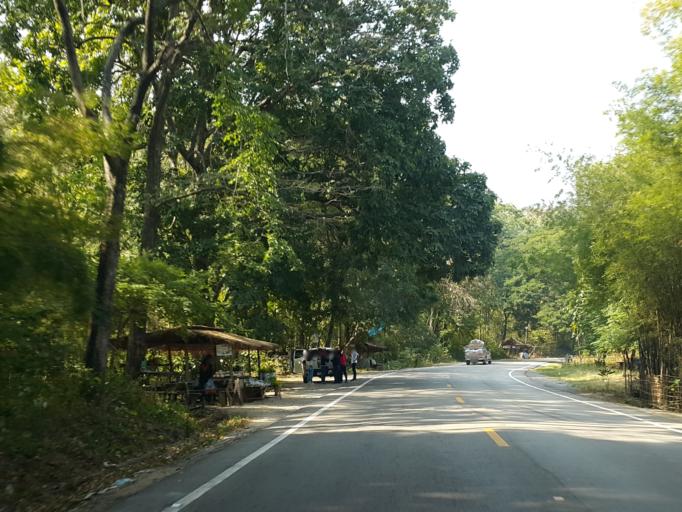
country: TH
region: Chiang Mai
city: Hot
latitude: 18.2278
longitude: 98.5643
